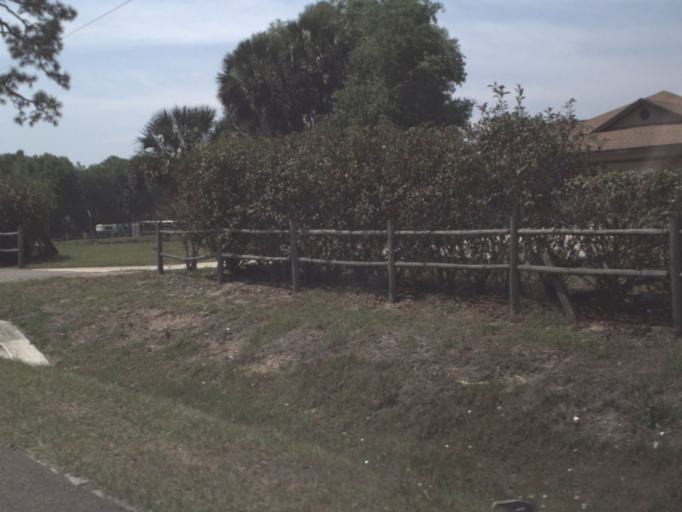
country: US
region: Florida
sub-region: Lake County
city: Umatilla
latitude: 28.9875
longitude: -81.6438
